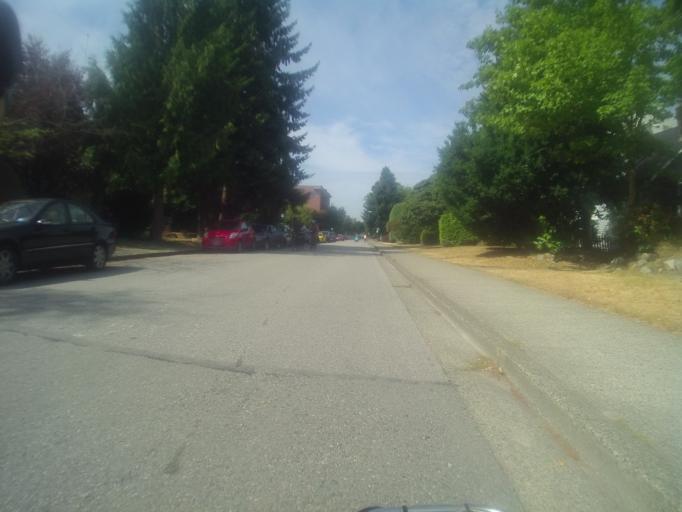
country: CA
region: British Columbia
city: Vancouver
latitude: 49.2626
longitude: -123.1318
